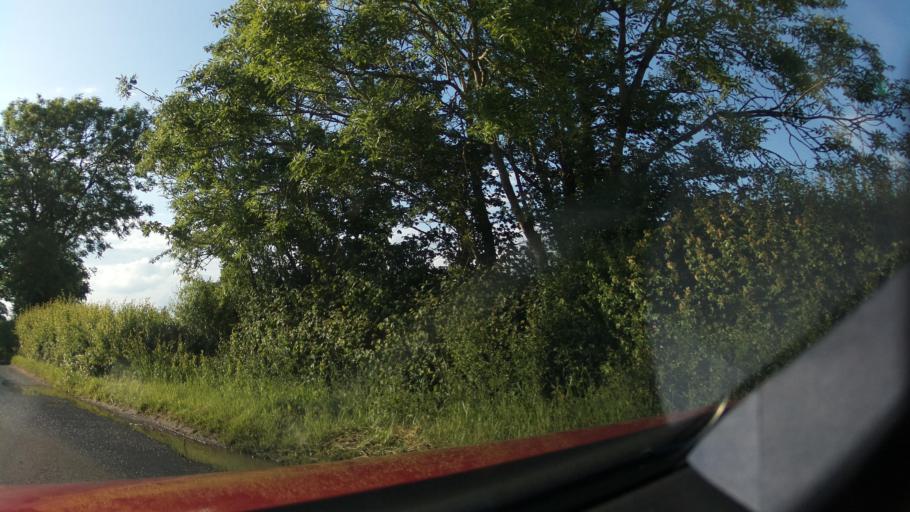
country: GB
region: England
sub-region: Lincolnshire
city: Navenby
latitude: 53.1164
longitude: -0.6220
